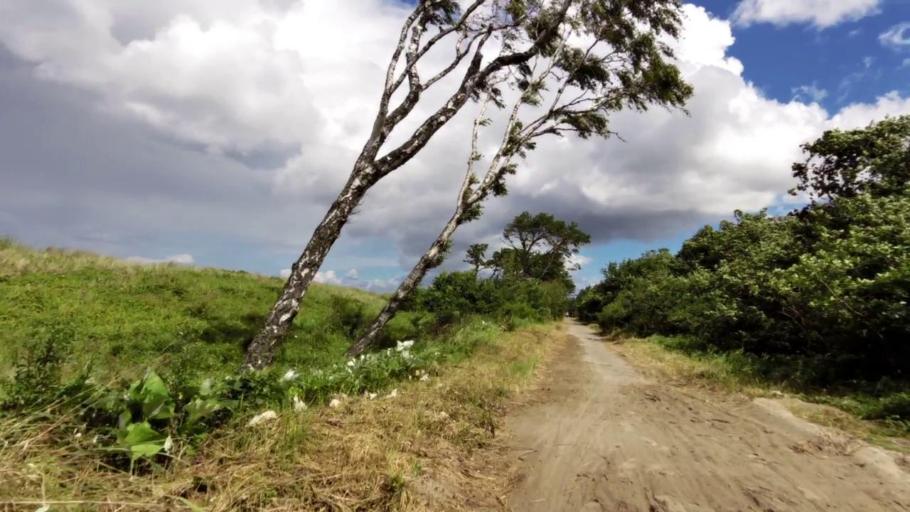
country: PL
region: West Pomeranian Voivodeship
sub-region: Powiat slawienski
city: Darlowo
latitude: 54.4938
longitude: 16.4440
